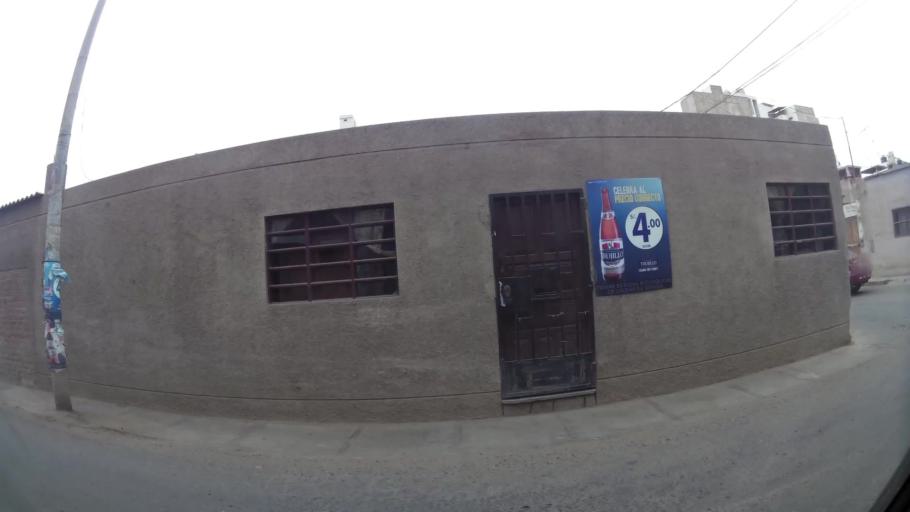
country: PE
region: La Libertad
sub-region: Provincia de Trujillo
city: Buenos Aires
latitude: -8.1369
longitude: -79.0394
